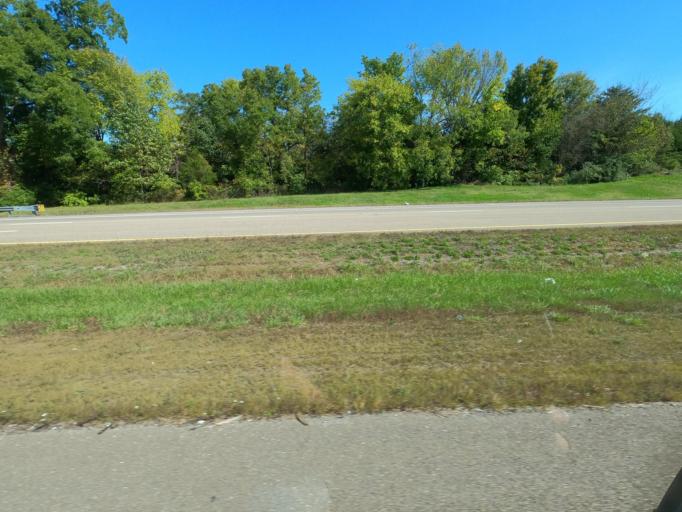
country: US
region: Tennessee
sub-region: Grainger County
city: Bean Station
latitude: 36.3404
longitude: -83.2925
